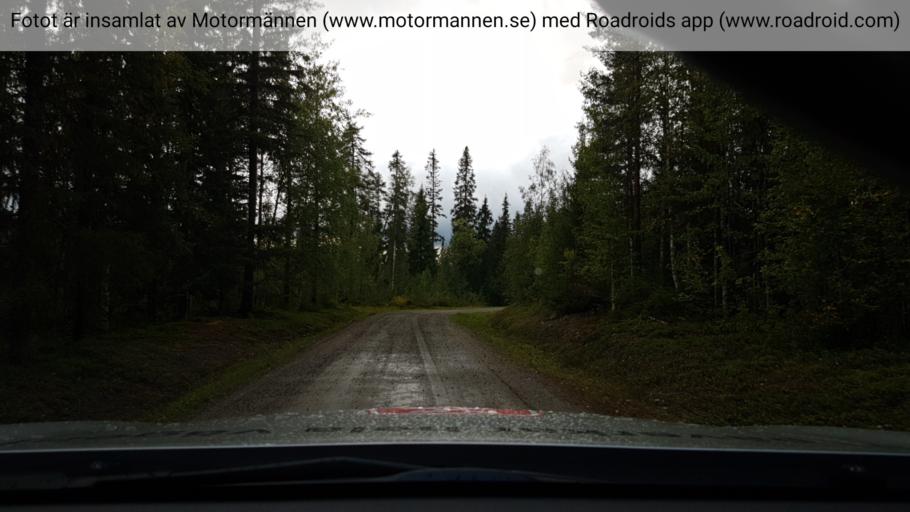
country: SE
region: Vaesterbotten
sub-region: Asele Kommun
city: Asele
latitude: 64.1481
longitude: 16.9320
